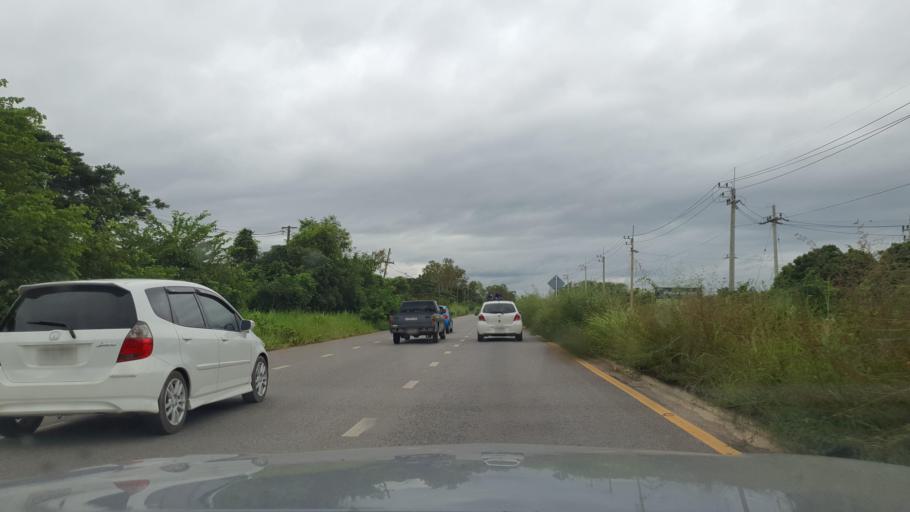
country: TH
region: Lamphun
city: Lamphun
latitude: 18.6012
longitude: 99.0082
